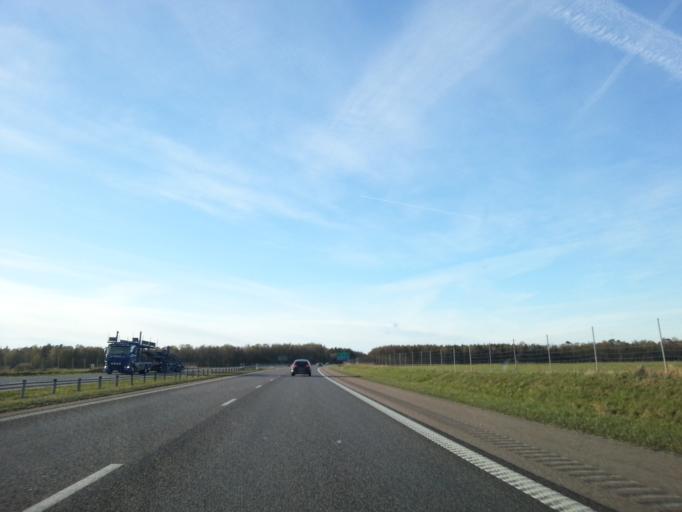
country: SE
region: Halland
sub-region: Laholms Kommun
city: Mellbystrand
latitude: 56.4594
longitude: 12.9439
